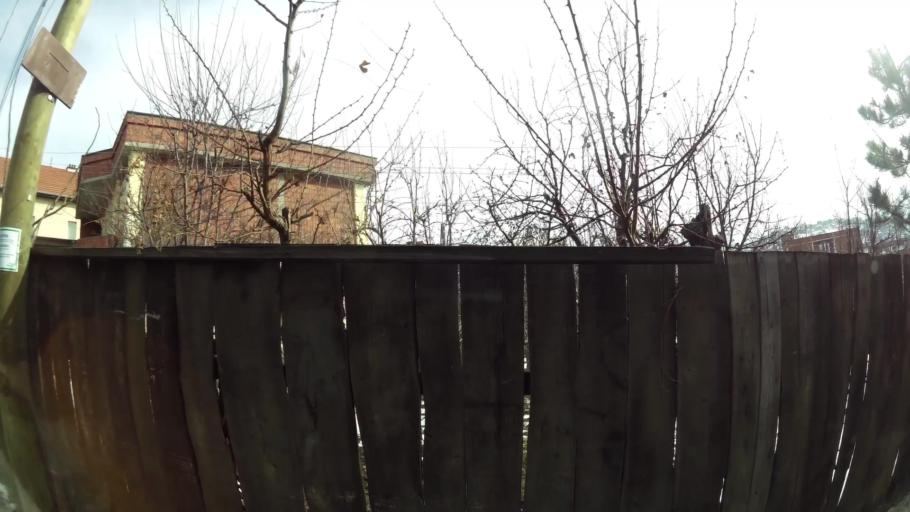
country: XK
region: Pristina
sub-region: Komuna e Prishtines
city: Pristina
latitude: 42.6823
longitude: 21.1694
